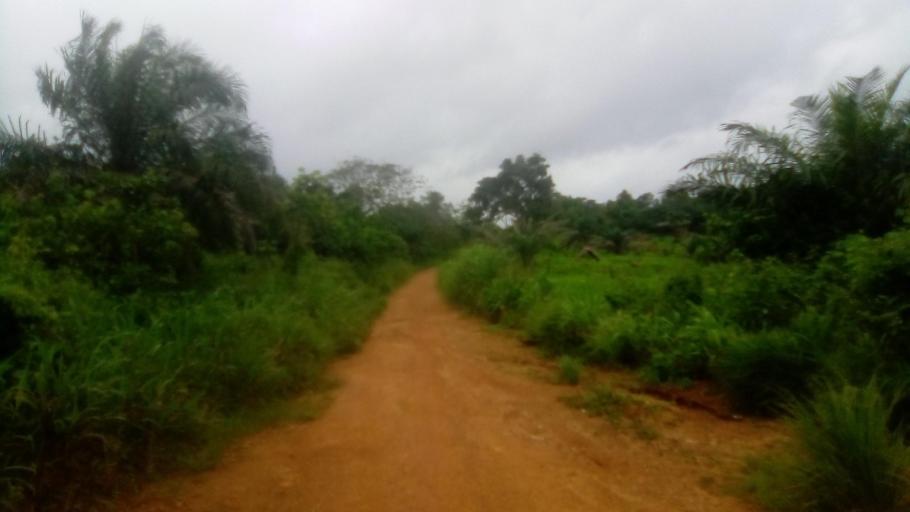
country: SL
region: Eastern Province
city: Kailahun
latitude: 8.2960
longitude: -10.5558
